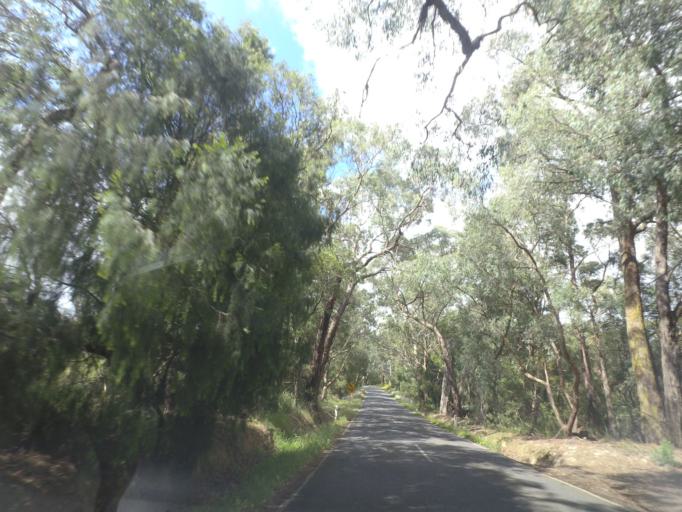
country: AU
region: Victoria
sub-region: Yarra Ranges
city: Launching Place
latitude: -37.7867
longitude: 145.5653
